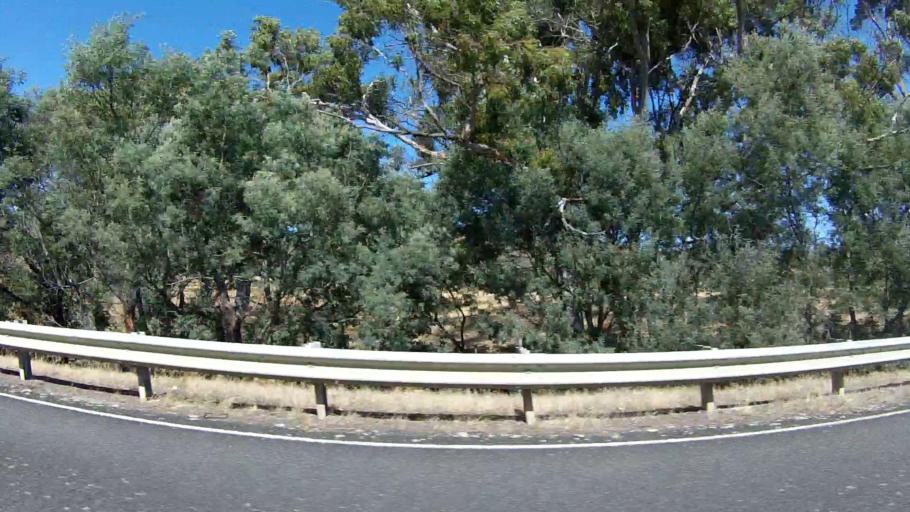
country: AU
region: Tasmania
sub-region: Sorell
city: Sorell
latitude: -42.5933
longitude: 147.7925
